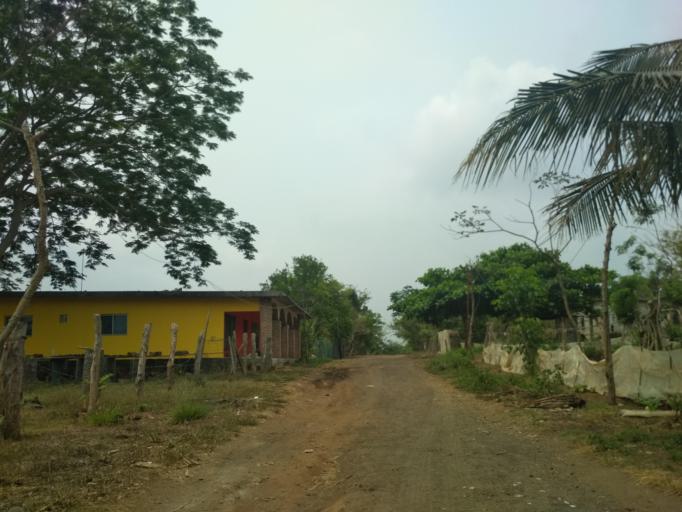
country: MX
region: Veracruz
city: Paso del Toro
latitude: 19.0219
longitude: -96.1377
